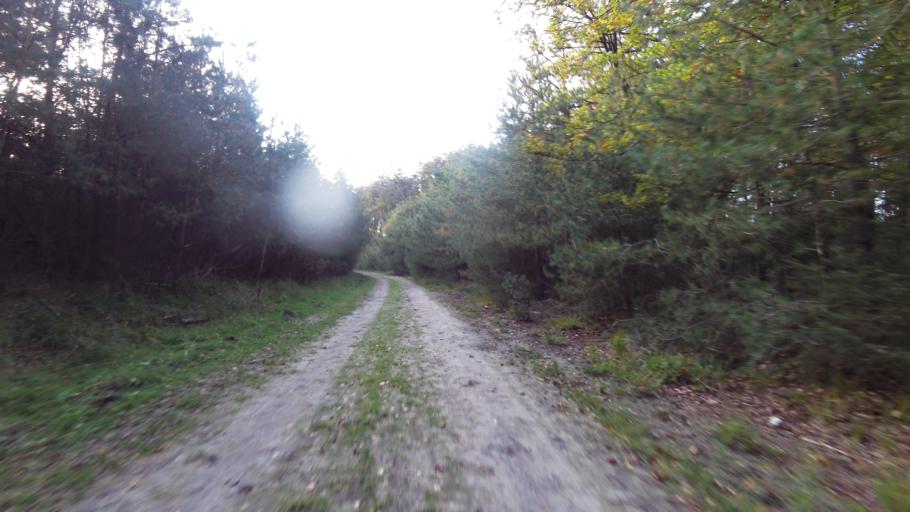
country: NL
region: Gelderland
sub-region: Gemeente Apeldoorn
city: Uddel
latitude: 52.3091
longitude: 5.8452
